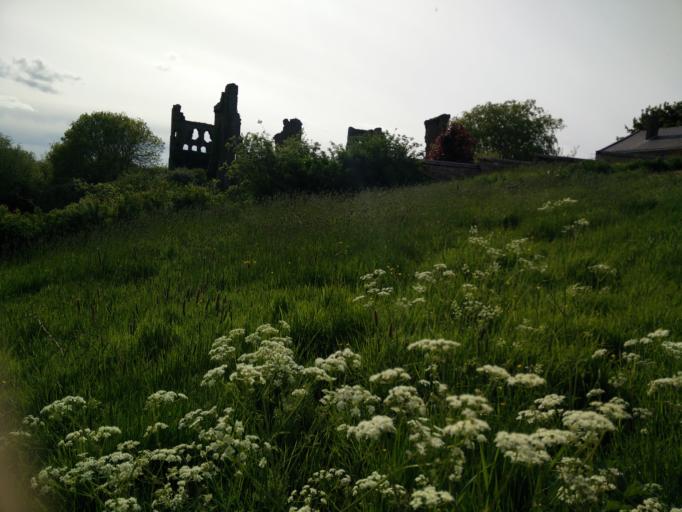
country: GB
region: England
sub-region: North Yorkshire
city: Strensall
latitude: 54.0879
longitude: -1.0026
